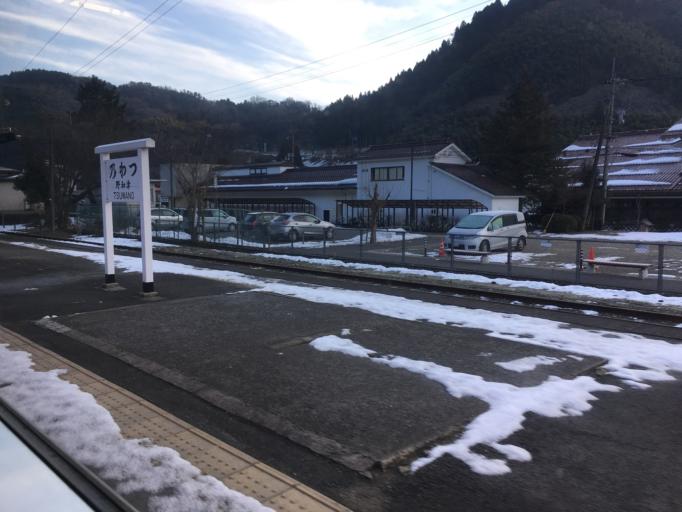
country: JP
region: Shimane
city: Masuda
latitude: 34.4720
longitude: 131.7736
